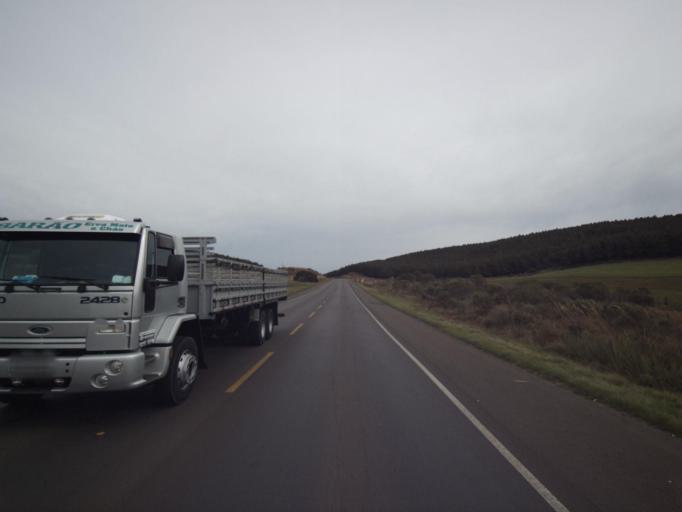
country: BR
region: Parana
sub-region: Palmas
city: Palmas
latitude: -26.6632
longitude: -51.5443
